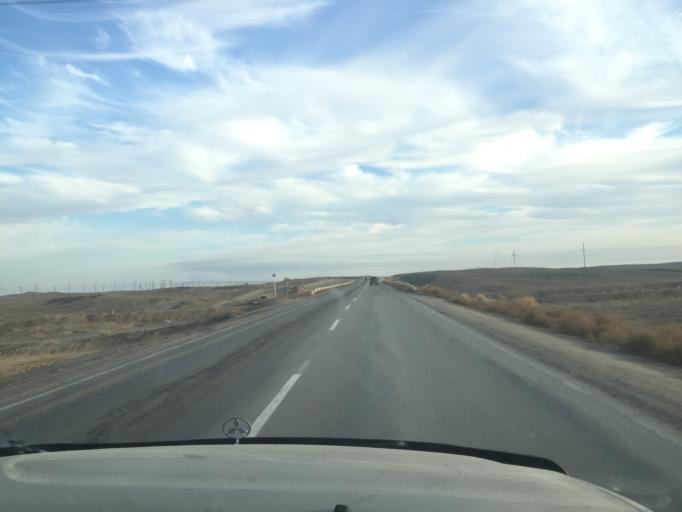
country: KZ
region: Almaty Oblysy
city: Ulken
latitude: 45.1895
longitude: 73.9150
